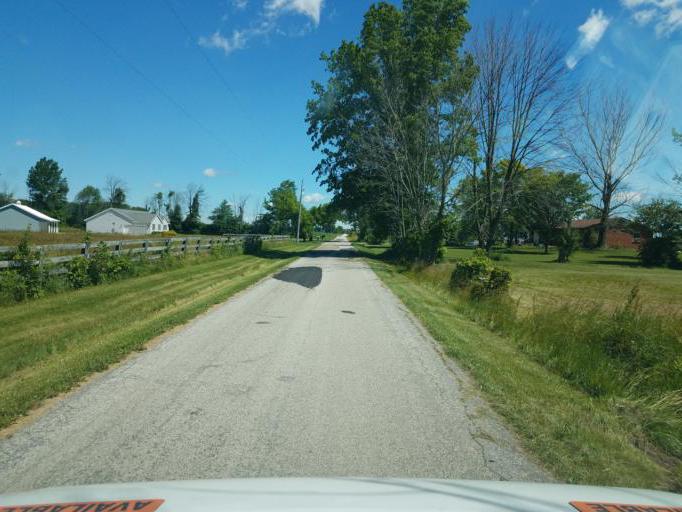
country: US
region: Ohio
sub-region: Morrow County
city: Cardington
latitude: 40.5256
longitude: -82.9341
